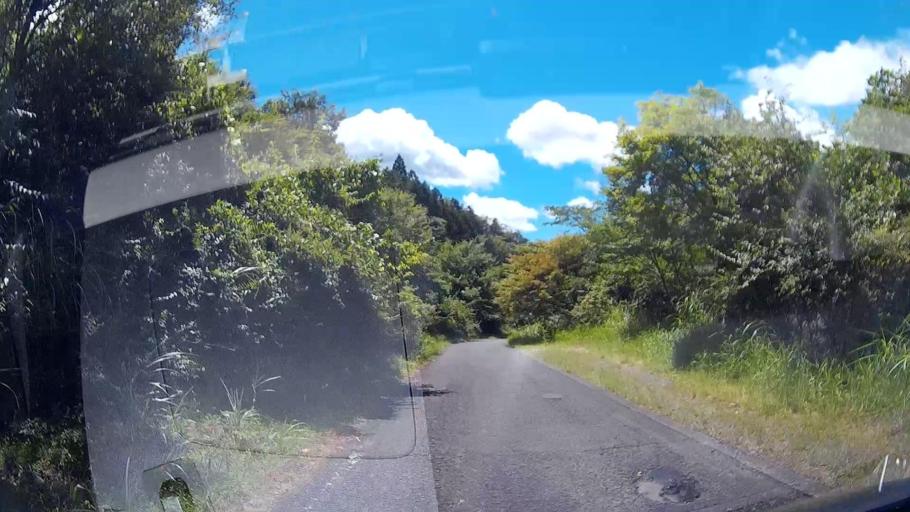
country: JP
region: Shizuoka
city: Fujinomiya
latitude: 35.2794
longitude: 138.3302
